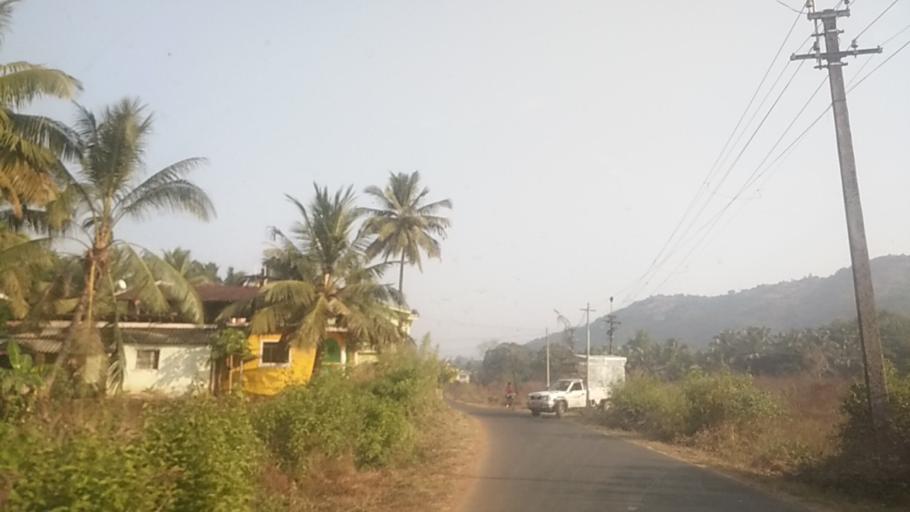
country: IN
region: Goa
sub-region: South Goa
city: Chinchinim
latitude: 15.2294
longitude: 73.9922
